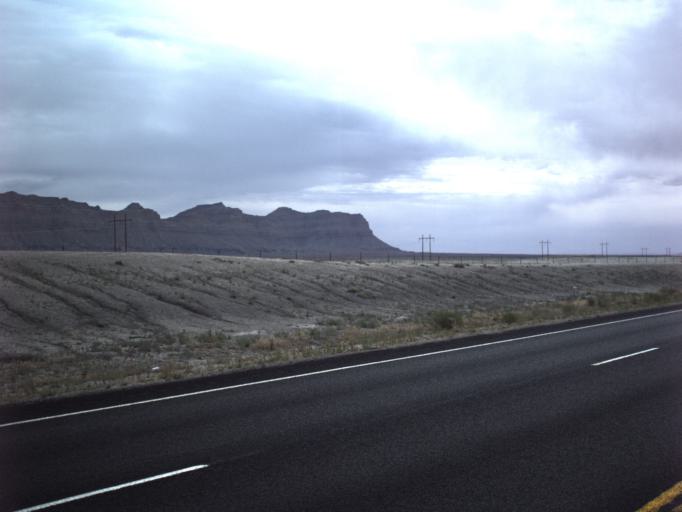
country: US
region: Utah
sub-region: Carbon County
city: East Carbon City
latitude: 39.1537
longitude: -110.3379
